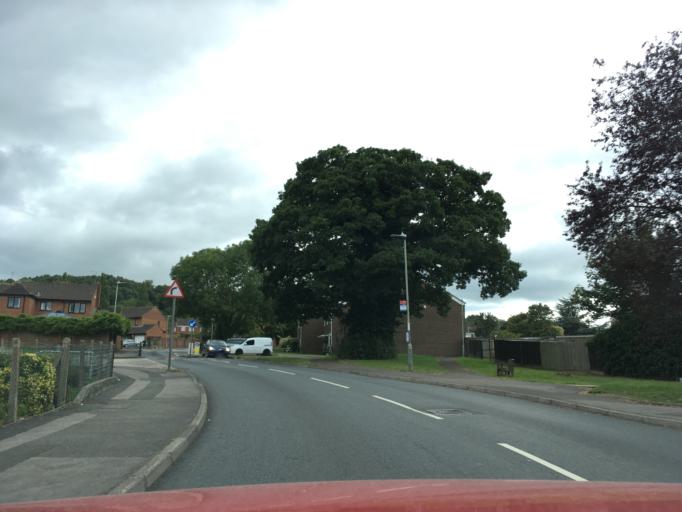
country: GB
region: England
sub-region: Gloucestershire
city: Barnwood
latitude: 51.8420
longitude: -2.2229
